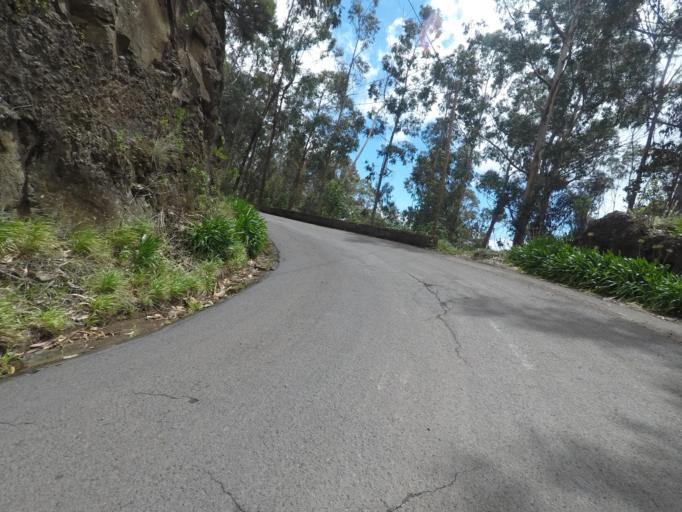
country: PT
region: Madeira
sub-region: Calheta
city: Estreito da Calheta
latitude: 32.7519
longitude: -17.1956
